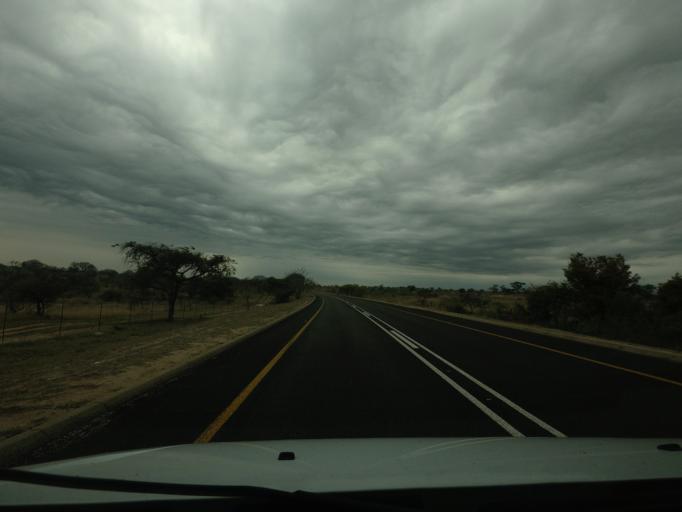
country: ZA
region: Limpopo
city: Thulamahashi
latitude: -24.5688
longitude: 31.0670
